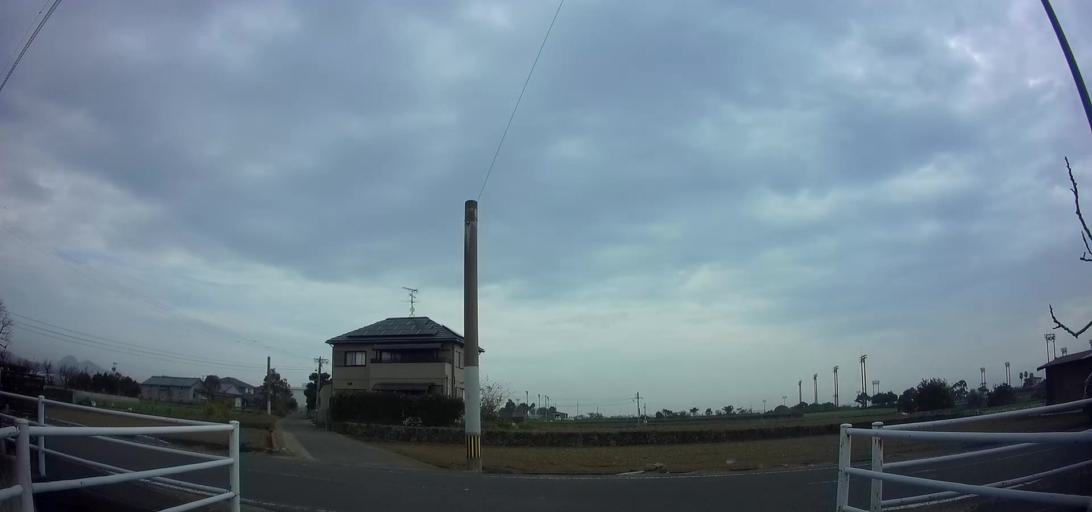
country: JP
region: Nagasaki
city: Shimabara
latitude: 32.6592
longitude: 130.3112
